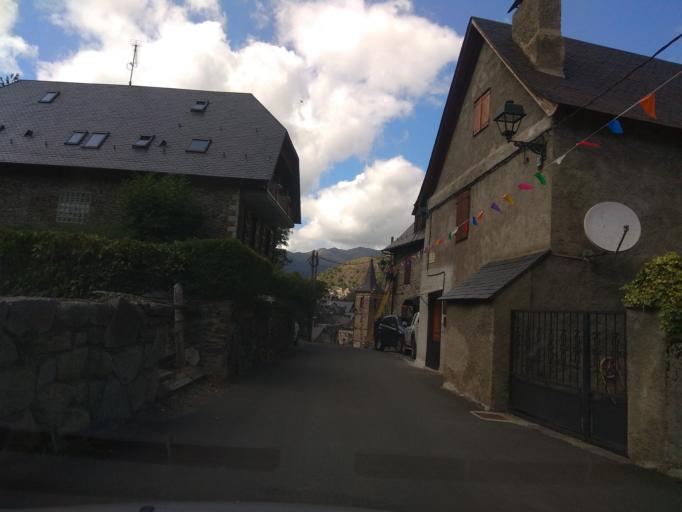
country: ES
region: Catalonia
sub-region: Provincia de Lleida
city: Les
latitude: 42.7369
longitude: 0.7201
